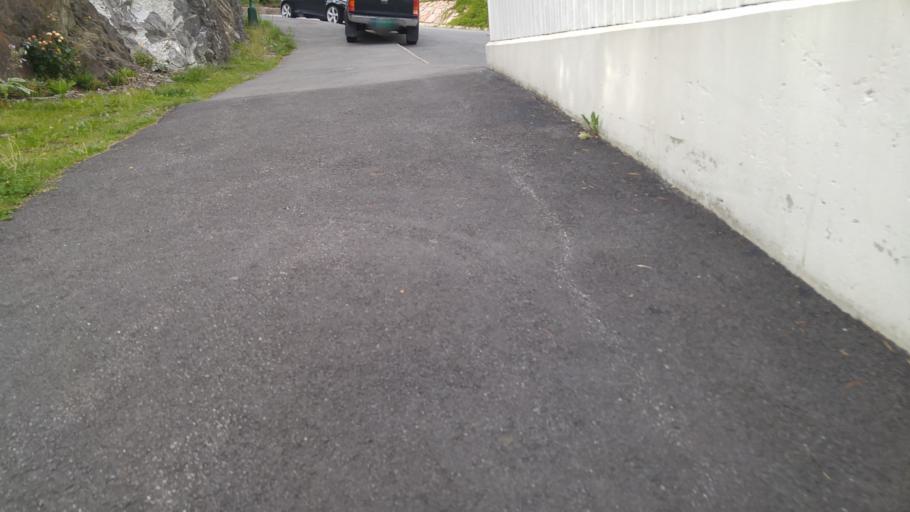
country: NO
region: Akershus
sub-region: Asker
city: Billingstad
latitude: 59.8512
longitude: 10.4947
